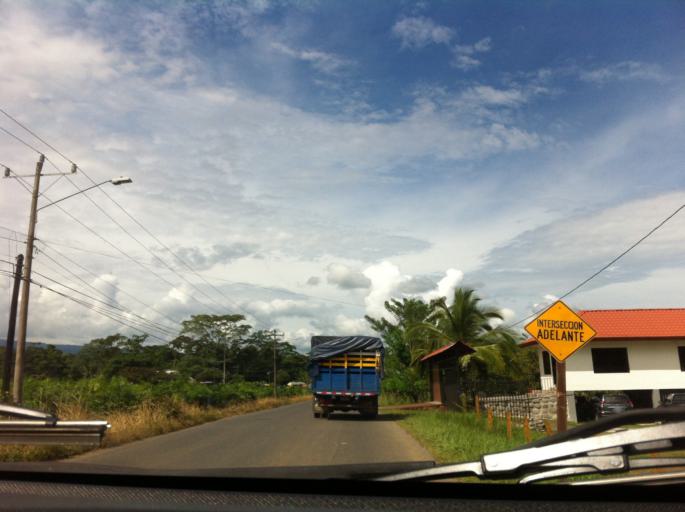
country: CR
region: San Jose
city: Dulce Nombre de Jesus
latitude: 10.3205
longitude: -83.9414
